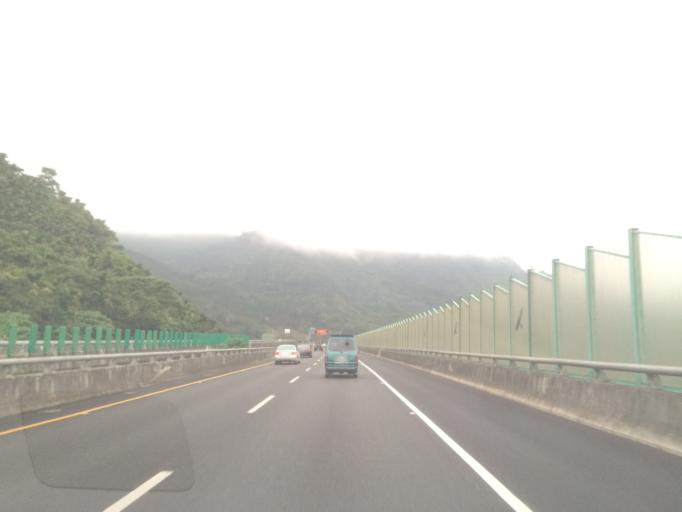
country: TW
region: Taiwan
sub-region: Nantou
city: Puli
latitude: 23.9967
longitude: 120.8493
